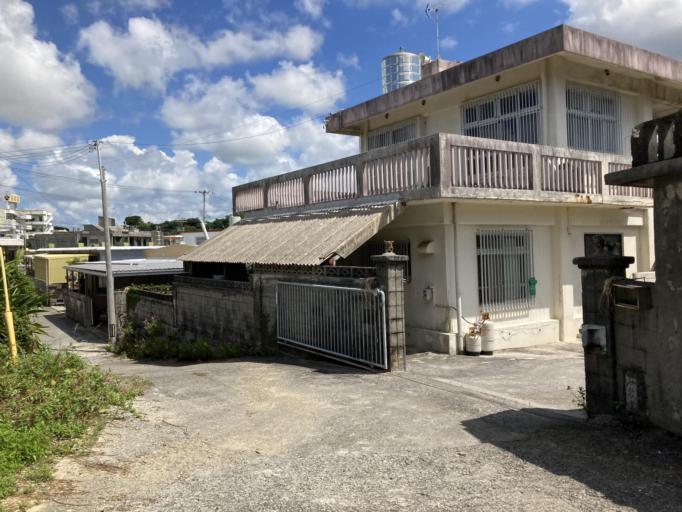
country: JP
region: Okinawa
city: Itoman
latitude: 26.1208
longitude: 127.7440
